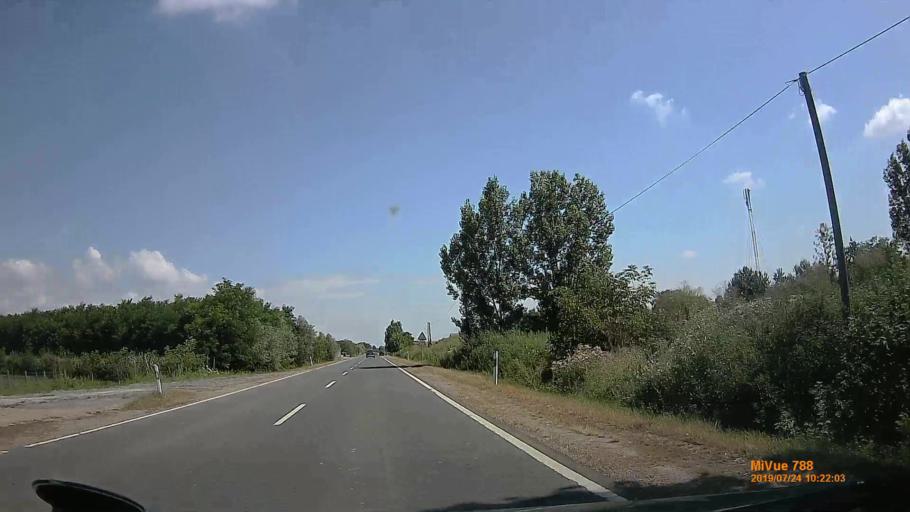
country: HU
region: Szabolcs-Szatmar-Bereg
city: Vasarosnameny
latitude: 48.1316
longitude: 22.3519
